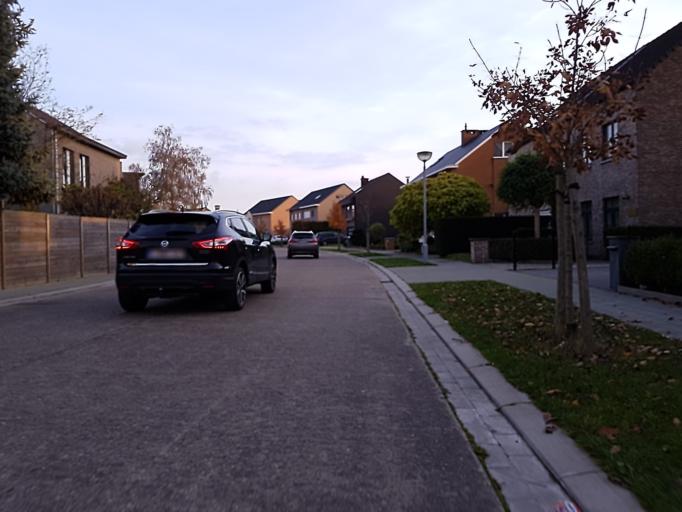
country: BE
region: Flanders
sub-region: Provincie Antwerpen
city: Ranst
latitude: 51.1919
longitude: 4.5551
